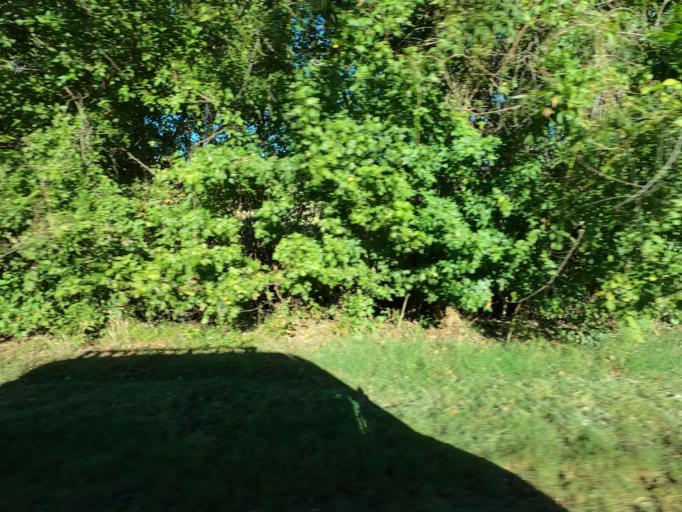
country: US
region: Tennessee
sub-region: Tipton County
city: Brighton
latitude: 35.5140
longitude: -89.7059
